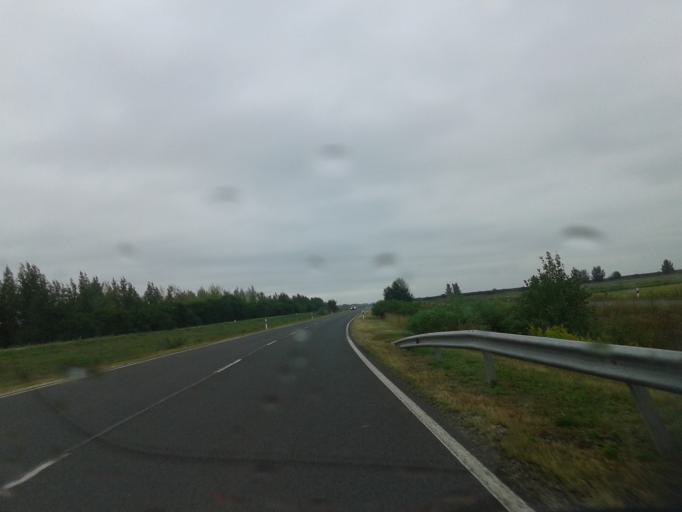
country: HU
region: Bacs-Kiskun
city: Harta
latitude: 46.7240
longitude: 19.0182
